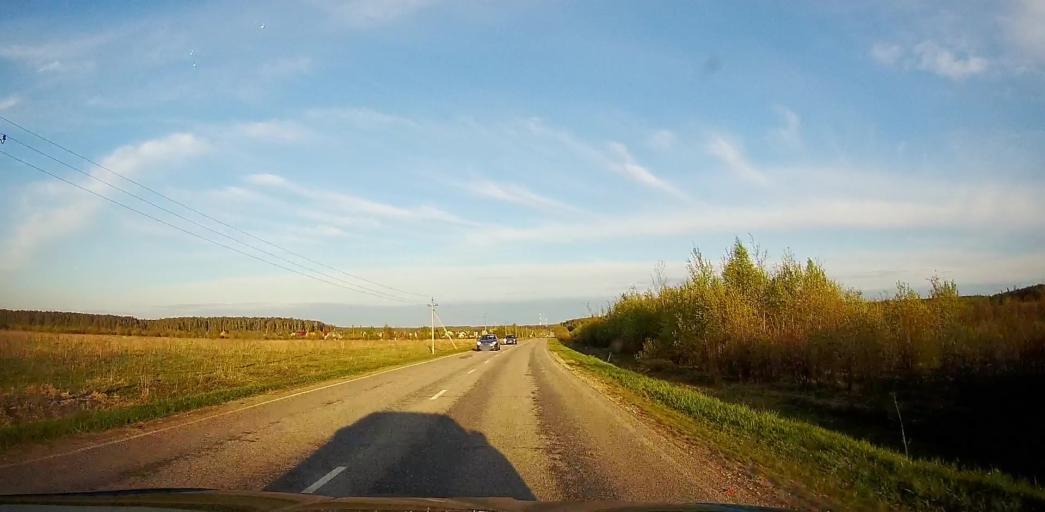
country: RU
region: Moskovskaya
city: Meshcherino
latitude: 55.2425
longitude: 38.3316
